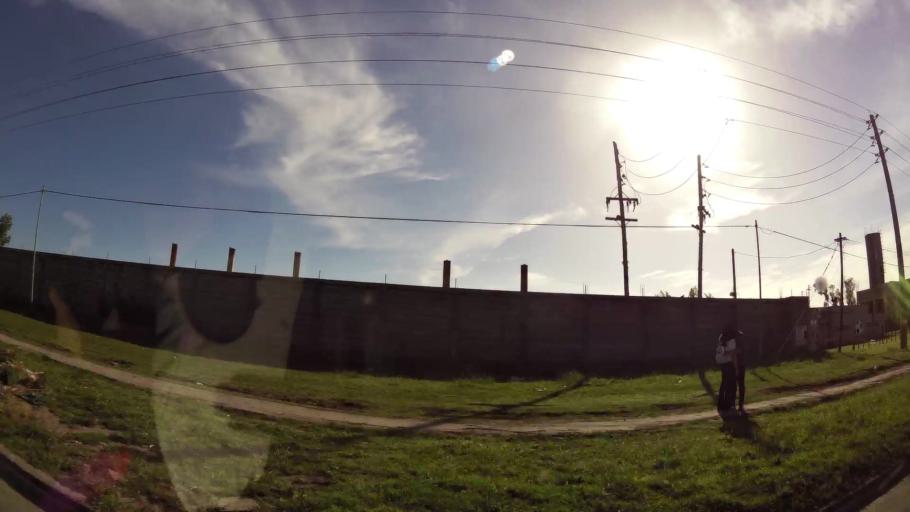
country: AR
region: Buenos Aires
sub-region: Partido de Quilmes
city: Quilmes
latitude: -34.7816
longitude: -58.2332
